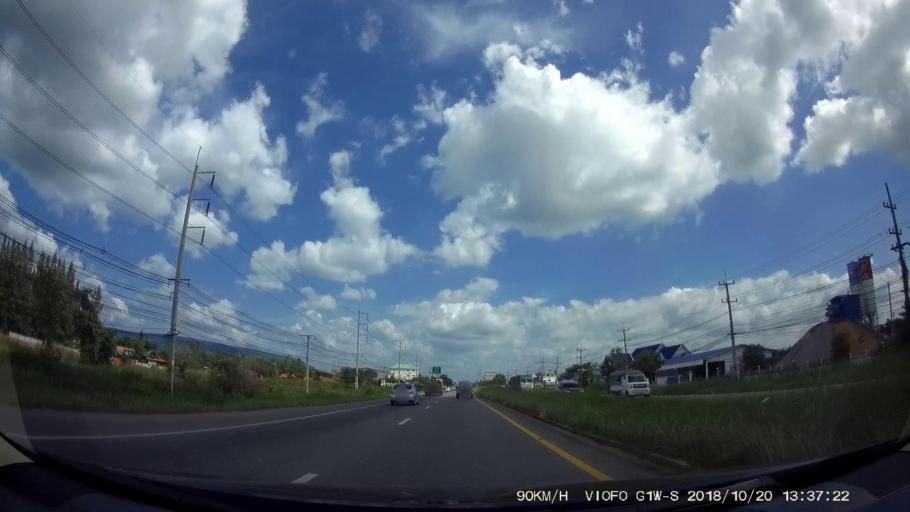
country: TH
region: Khon Kaen
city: Chum Phae
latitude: 16.5584
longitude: 102.0699
